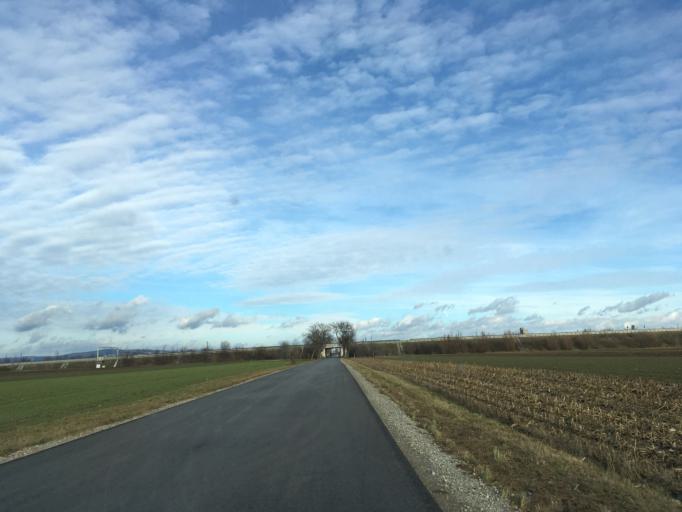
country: AT
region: Burgenland
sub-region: Politischer Bezirk Neusiedl am See
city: Kittsee
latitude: 48.0726
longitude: 17.0574
